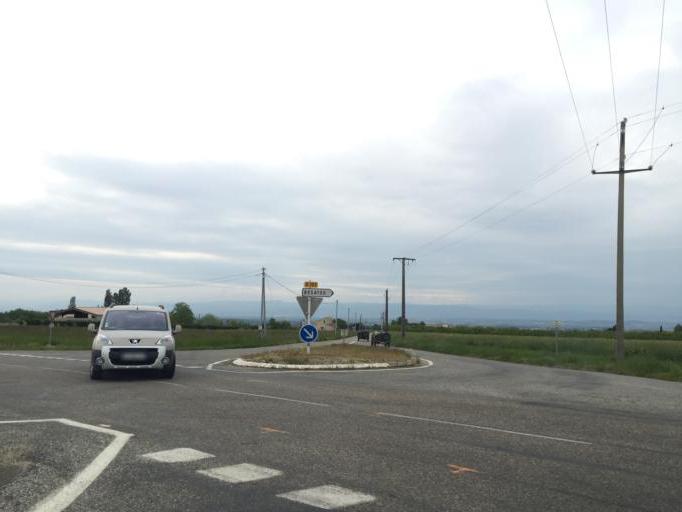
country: FR
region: Rhone-Alpes
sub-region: Departement de la Drome
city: Chatuzange-le-Goubet
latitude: 44.9565
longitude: 5.1279
